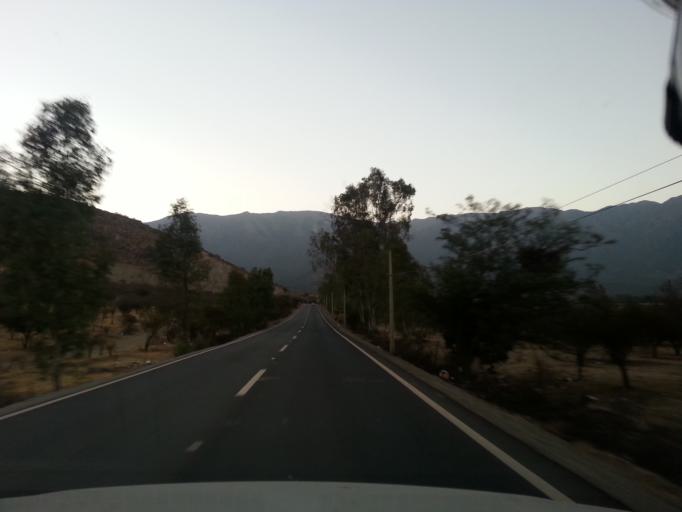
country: CL
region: Santiago Metropolitan
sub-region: Provincia de Chacabuco
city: Lampa
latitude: -33.2452
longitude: -70.9173
